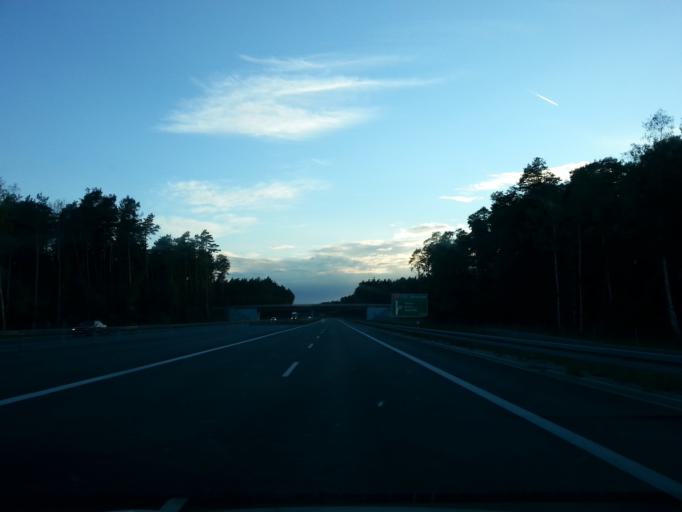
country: PL
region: Greater Poland Voivodeship
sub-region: Powiat kepinski
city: Bralin
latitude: 51.2999
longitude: 17.8886
